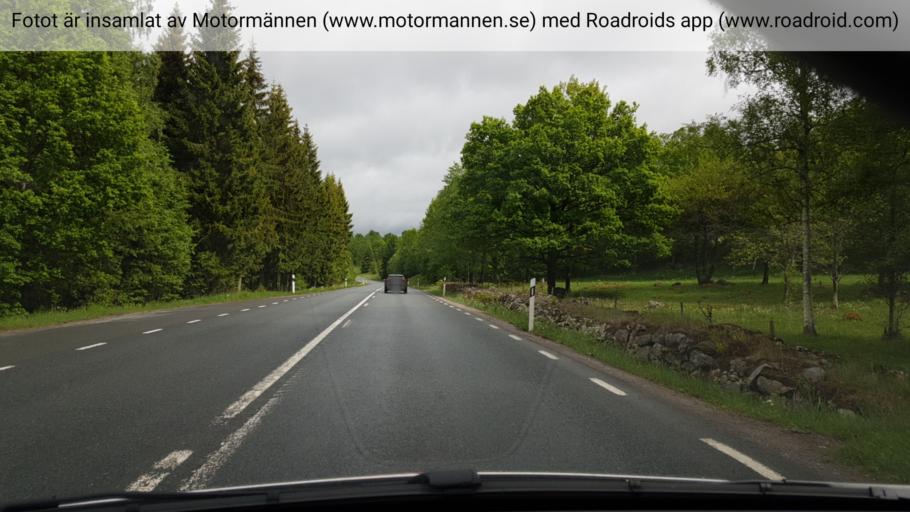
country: SE
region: Joenkoeping
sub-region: Aneby Kommun
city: Aneby
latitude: 57.8765
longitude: 14.8762
